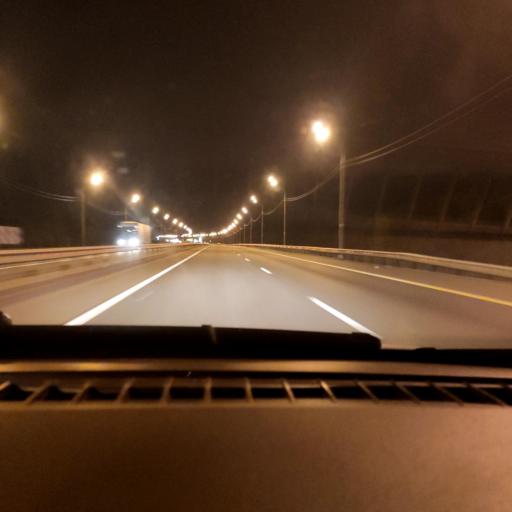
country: RU
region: Lipetsk
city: Khlevnoye
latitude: 52.2714
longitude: 39.0572
